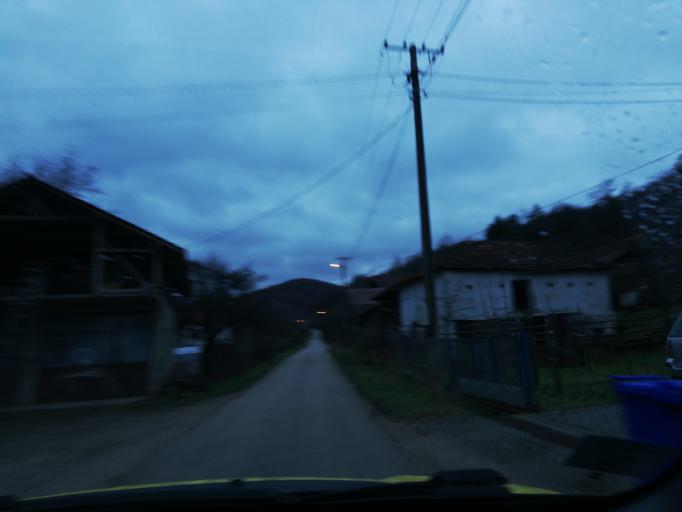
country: RS
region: Central Serbia
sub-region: Pirotski Okrug
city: Dimitrovgrad
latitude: 43.0112
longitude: 22.7210
